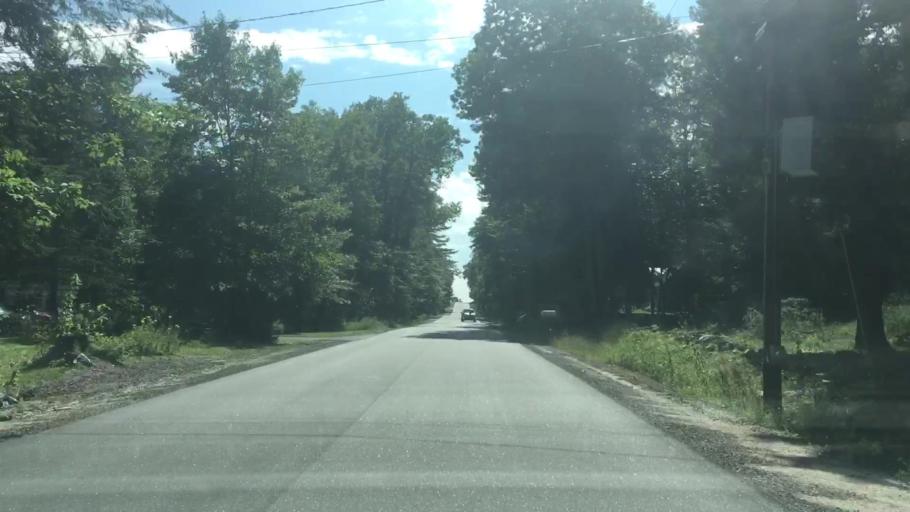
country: US
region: Maine
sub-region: Androscoggin County
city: Poland
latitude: 44.0083
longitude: -70.3681
